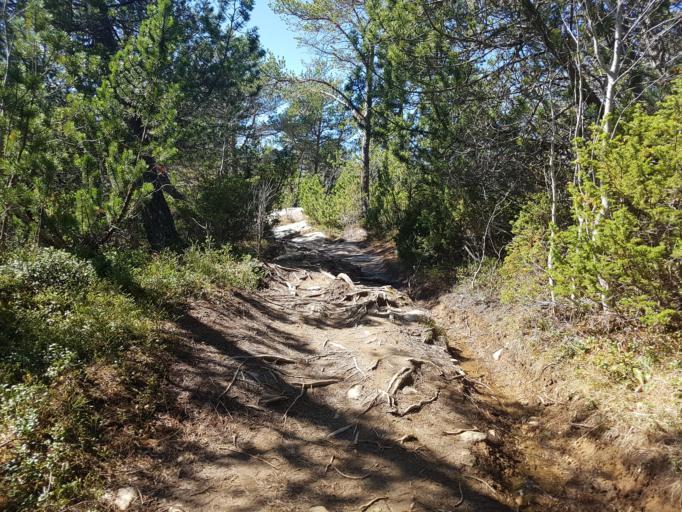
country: NO
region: Sor-Trondelag
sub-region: Trondheim
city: Trondheim
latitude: 63.4357
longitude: 10.3257
